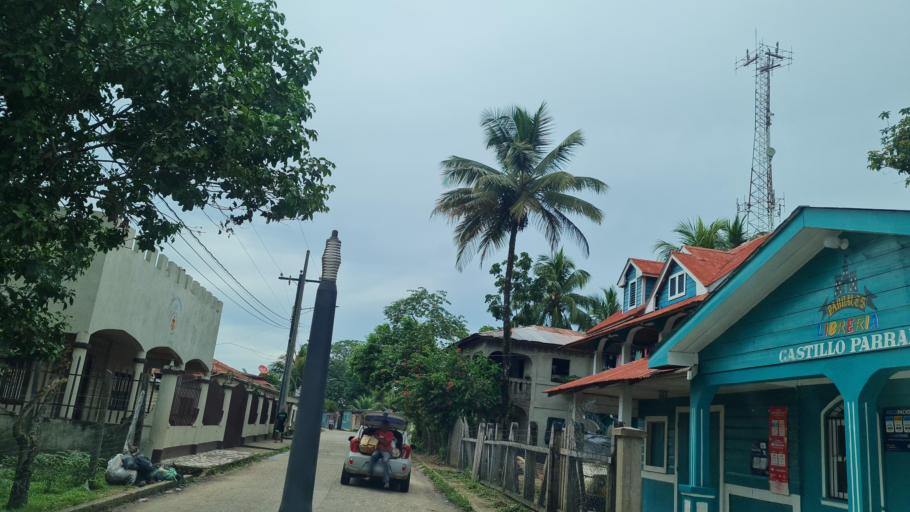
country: NI
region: Atlantico Norte (RAAN)
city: Waspam
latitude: 14.7408
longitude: -83.9717
